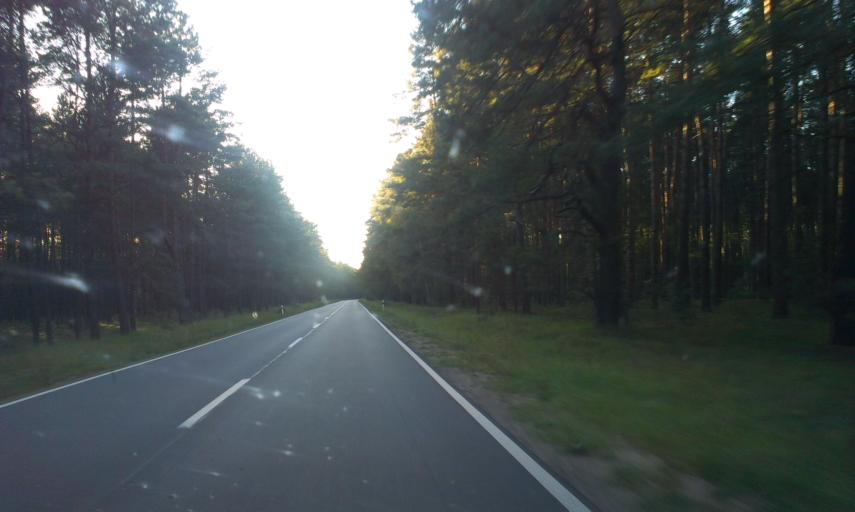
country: PL
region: Pomeranian Voivodeship
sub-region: Powiat czluchowski
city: Czarne
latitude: 53.6927
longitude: 16.9109
